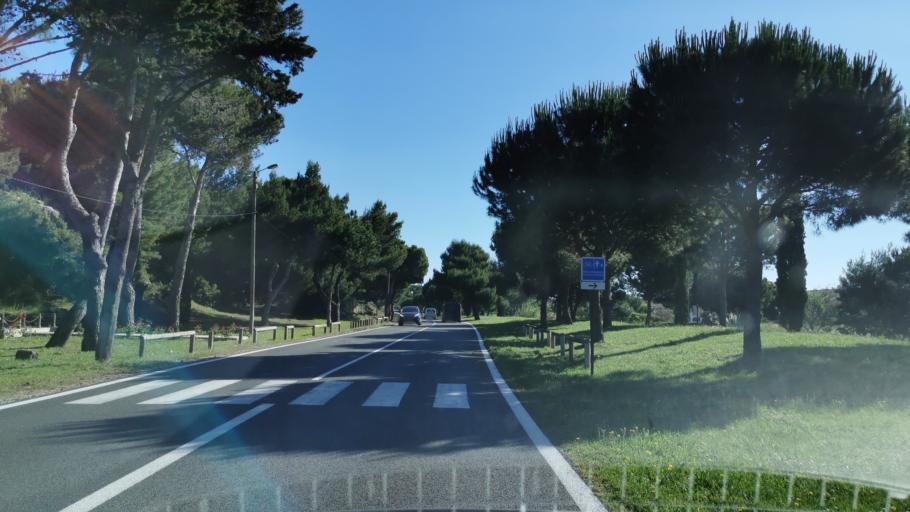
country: FR
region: Languedoc-Roussillon
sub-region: Departement de l'Aude
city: Armissan
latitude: 43.1572
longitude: 3.1586
